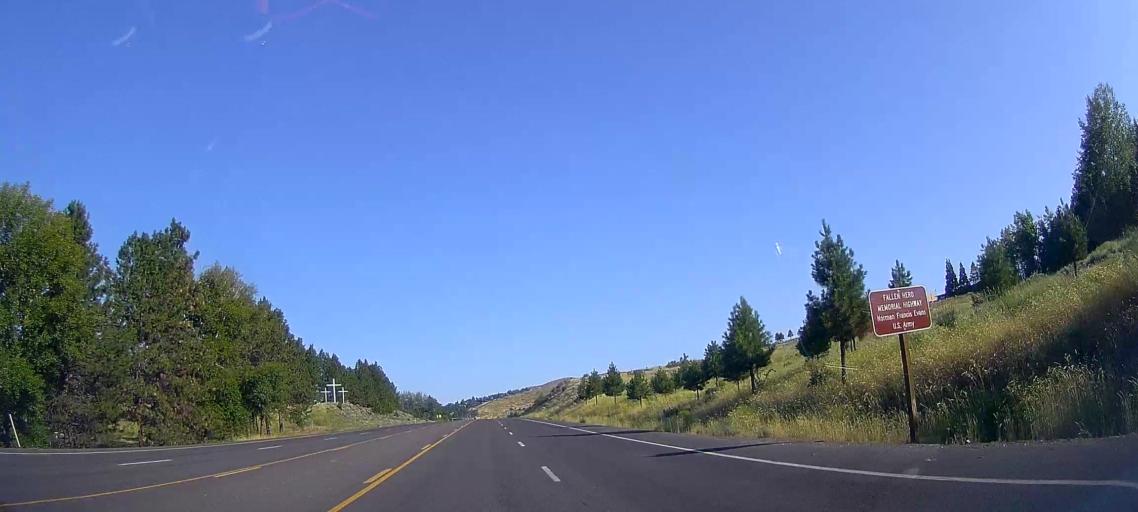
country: US
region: Oregon
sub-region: Klamath County
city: Altamont
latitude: 42.2191
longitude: -121.7493
